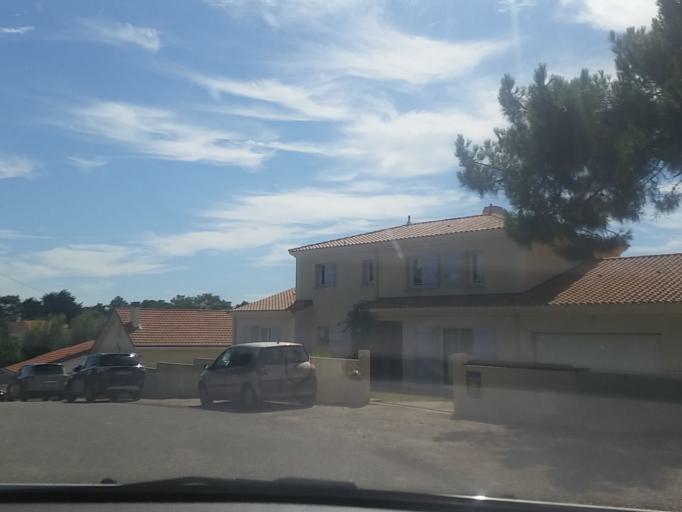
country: FR
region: Pays de la Loire
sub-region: Departement de la Loire-Atlantique
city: Saint-Michel-Chef-Chef
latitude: 47.1725
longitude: -2.1631
